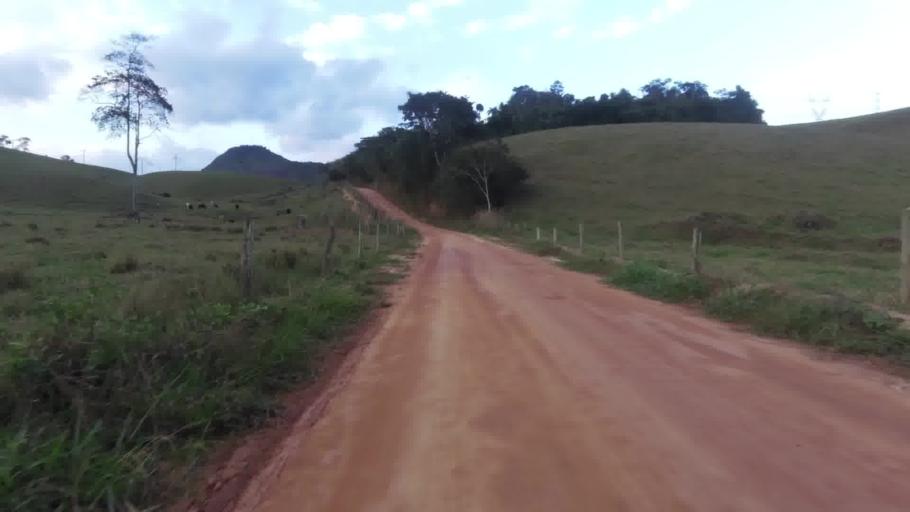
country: BR
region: Espirito Santo
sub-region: Guarapari
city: Guarapari
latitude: -20.6703
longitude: -40.6114
